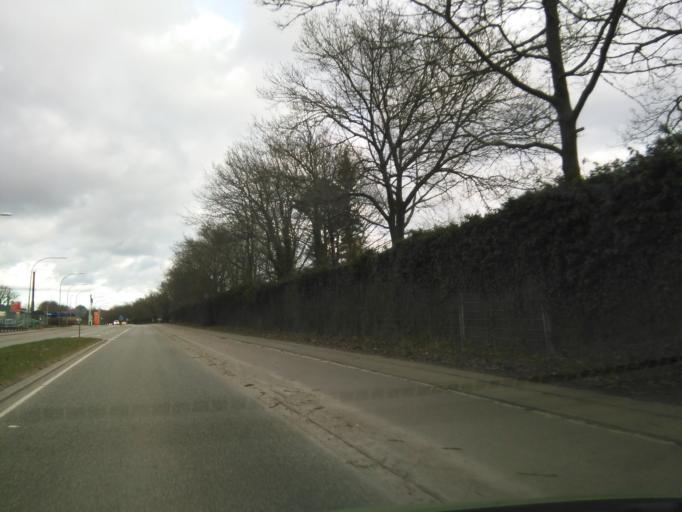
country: DK
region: Central Jutland
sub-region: Arhus Kommune
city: Stavtrup
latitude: 56.1630
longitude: 10.1224
